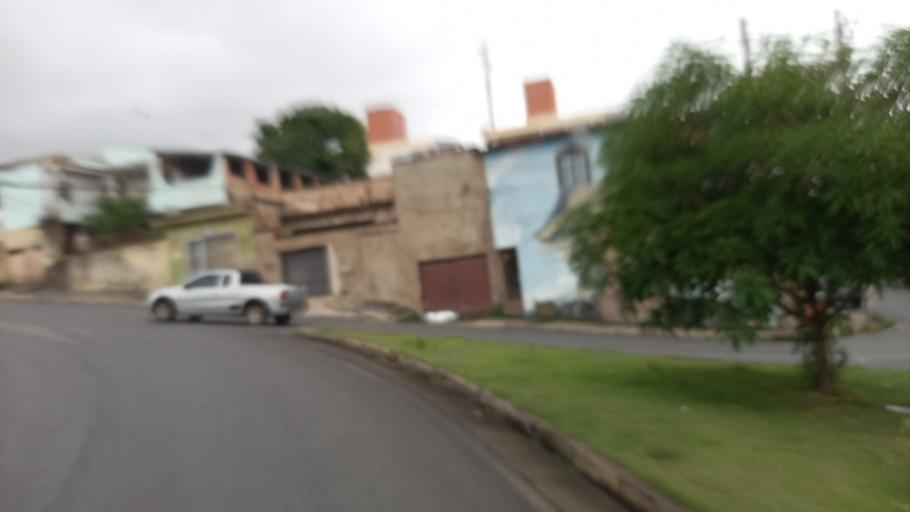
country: BR
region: Minas Gerais
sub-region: Belo Horizonte
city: Belo Horizonte
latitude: -19.8804
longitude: -43.9124
